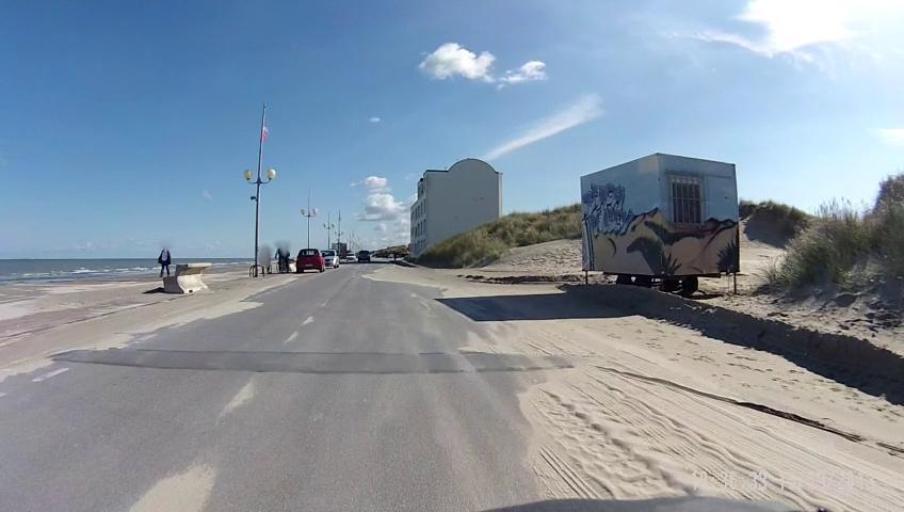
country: FR
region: Nord-Pas-de-Calais
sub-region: Departement du Nord
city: Leffrinckoucke
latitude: 51.0585
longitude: 2.4359
